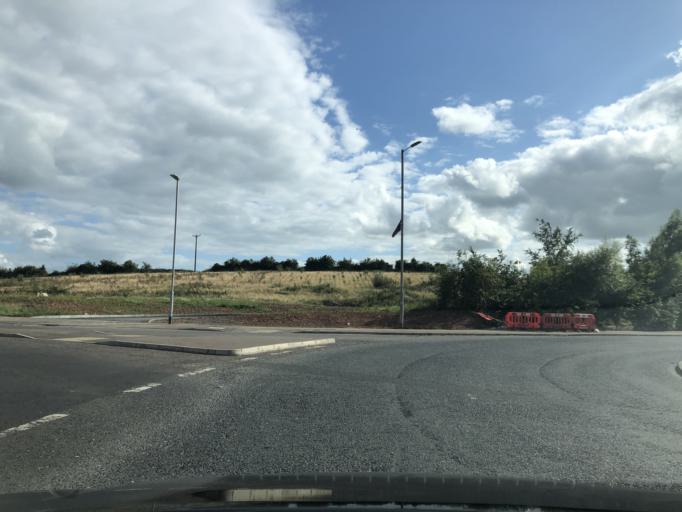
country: GB
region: Northern Ireland
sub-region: Ards District
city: Comber
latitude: 54.5513
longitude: -5.7292
